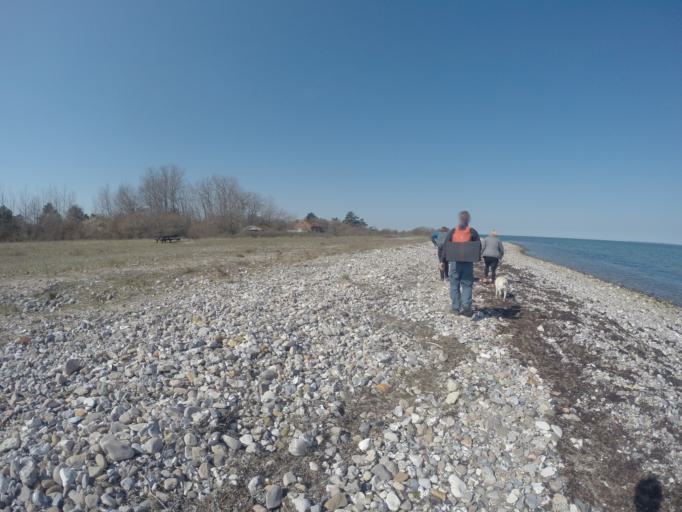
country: DK
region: Zealand
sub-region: Kalundborg Kommune
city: Gorlev
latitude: 55.5363
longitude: 11.1271
